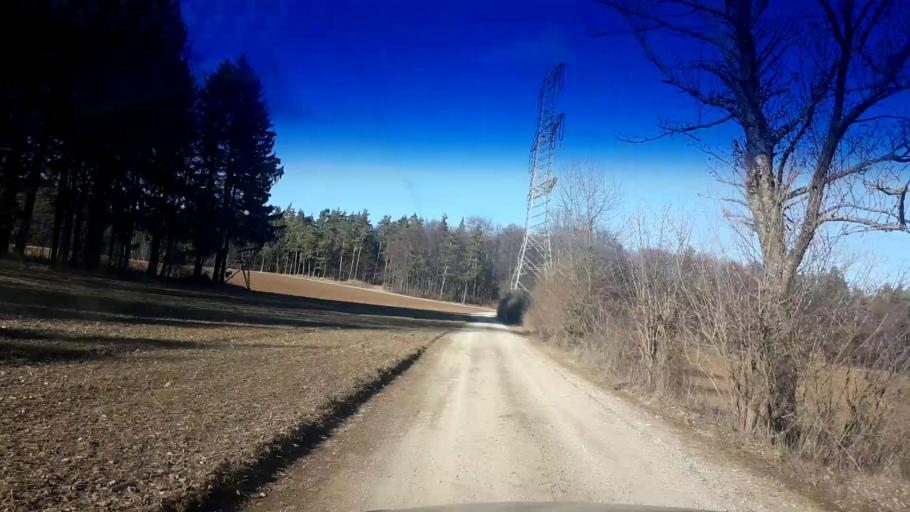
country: DE
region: Bavaria
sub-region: Upper Franconia
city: Poxdorf
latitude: 49.9651
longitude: 11.0857
